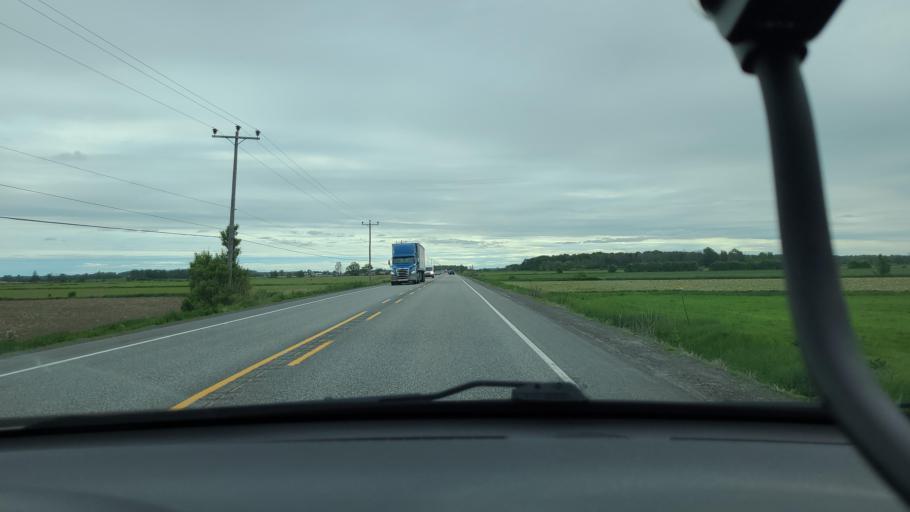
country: CA
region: Quebec
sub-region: Lanaudiere
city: Sainte-Julienne
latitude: 45.9136
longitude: -73.6513
